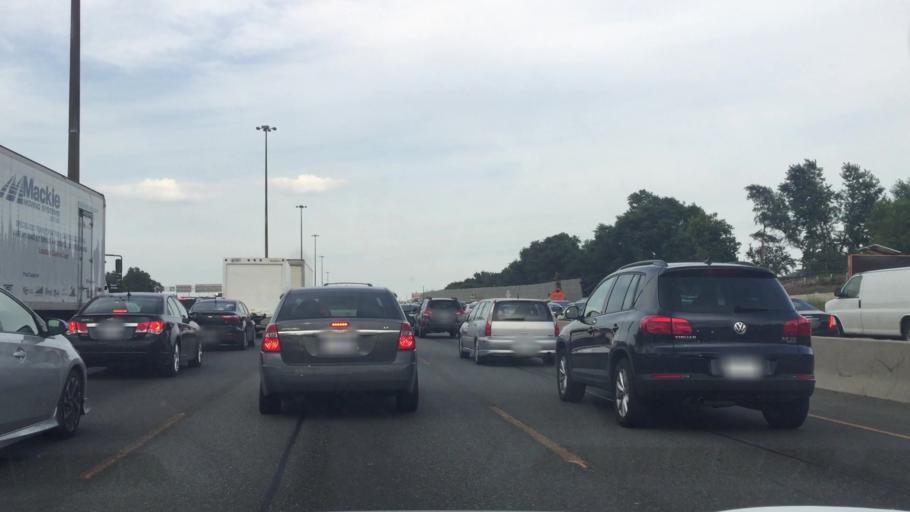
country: CA
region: Ontario
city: Toronto
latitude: 43.7223
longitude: -79.4784
